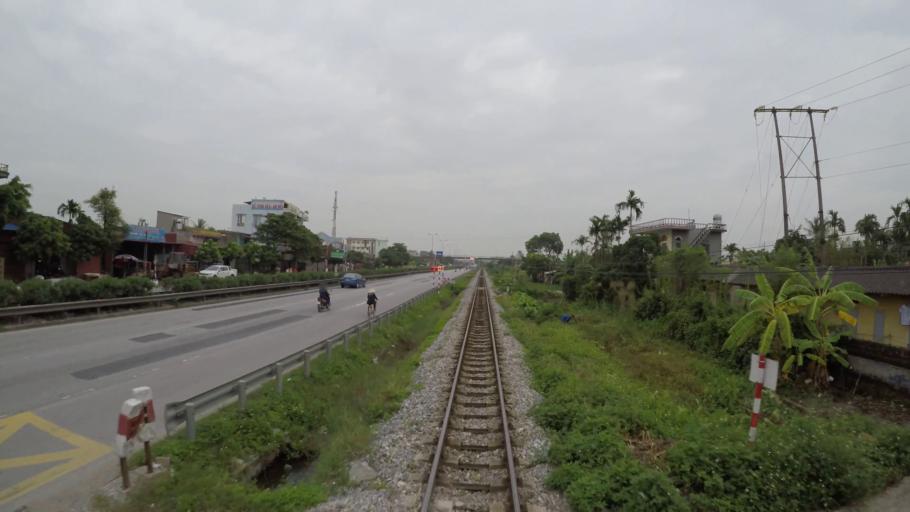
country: VN
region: Hai Duong
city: Phu Thai
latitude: 20.9718
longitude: 106.4726
